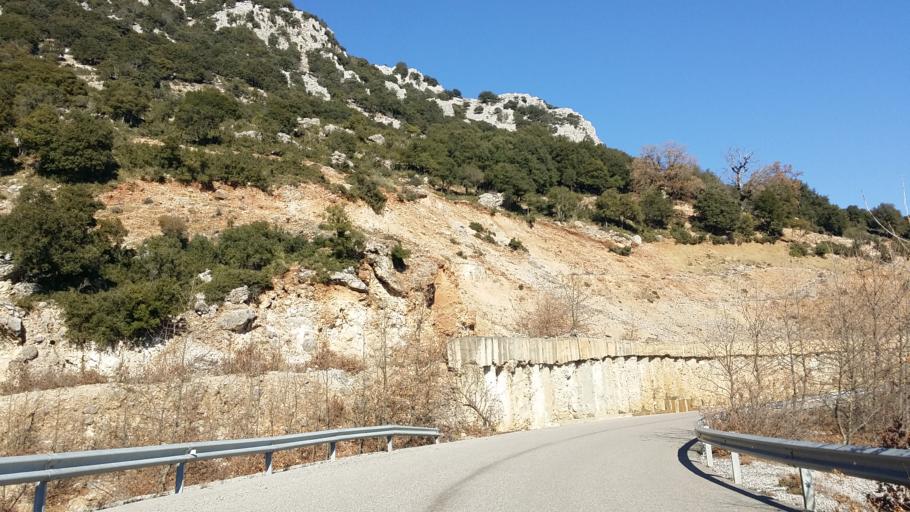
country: GR
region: Central Greece
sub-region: Nomos Evrytanias
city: Kerasochori
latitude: 38.9463
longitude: 21.4591
